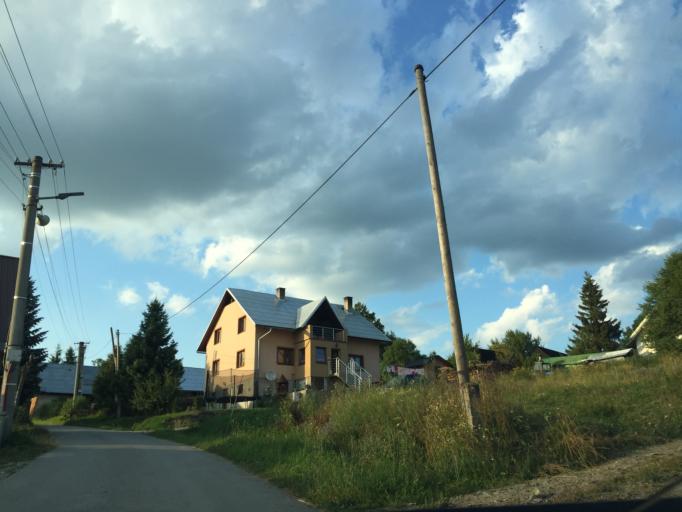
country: PL
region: Silesian Voivodeship
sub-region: Powiat zywiecki
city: Korbielow
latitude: 49.4856
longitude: 19.3819
